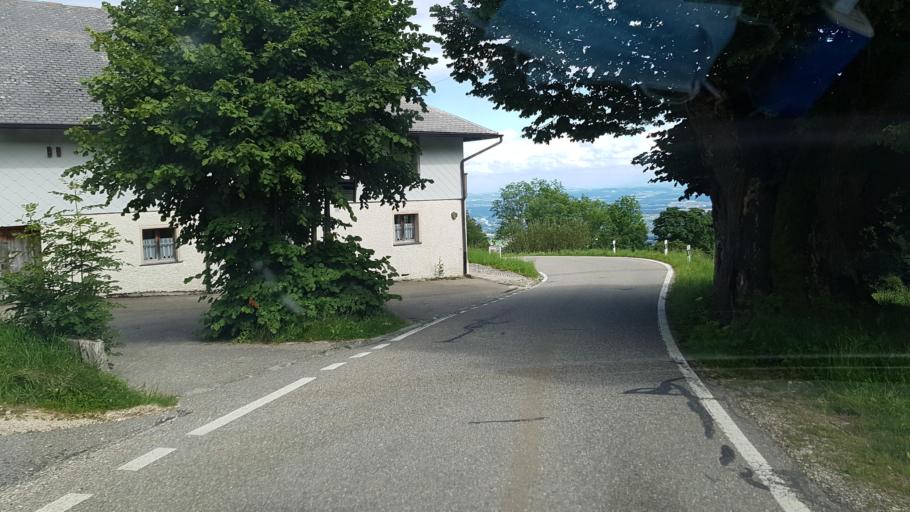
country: CH
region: Solothurn
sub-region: Bezirk Thal
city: Welschenrohr
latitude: 47.2623
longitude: 7.5438
